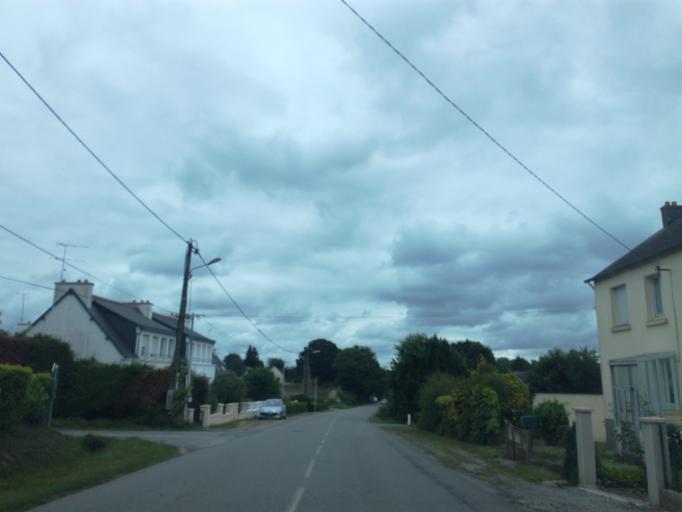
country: FR
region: Brittany
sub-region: Departement du Morbihan
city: Cleguerec
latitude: 48.1184
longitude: -3.0574
